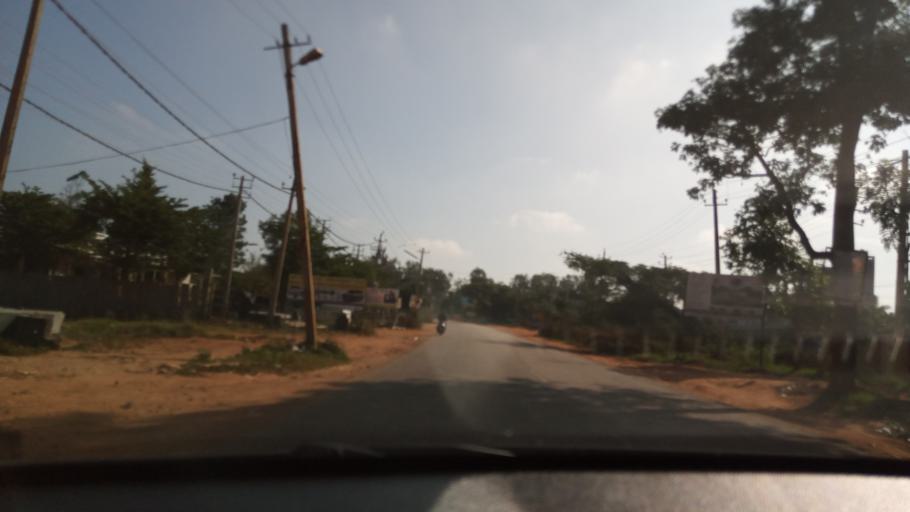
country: IN
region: Karnataka
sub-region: Bangalore Rural
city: Devanhalli
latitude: 13.2568
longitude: 77.7242
